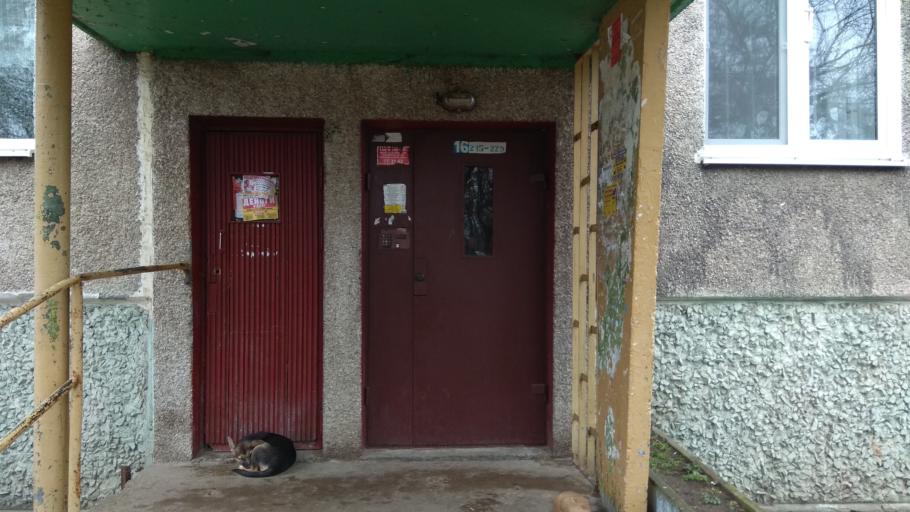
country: BY
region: Grodnenskaya
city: Hrodna
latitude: 53.7077
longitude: 23.7961
